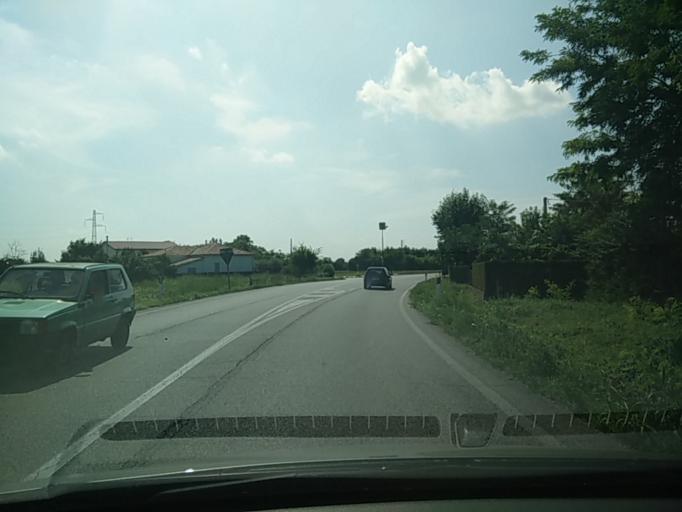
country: IT
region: Veneto
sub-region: Provincia di Treviso
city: Lancenigo-Villorba
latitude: 45.7075
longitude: 12.2698
